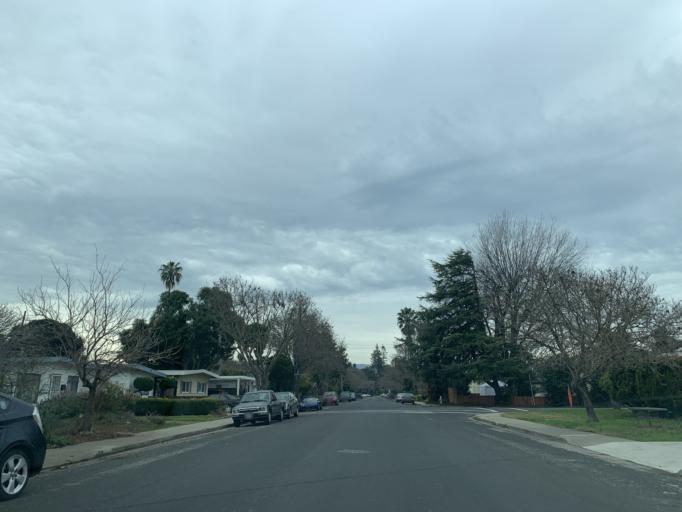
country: US
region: California
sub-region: Santa Clara County
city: Mountain View
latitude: 37.4050
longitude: -122.0655
